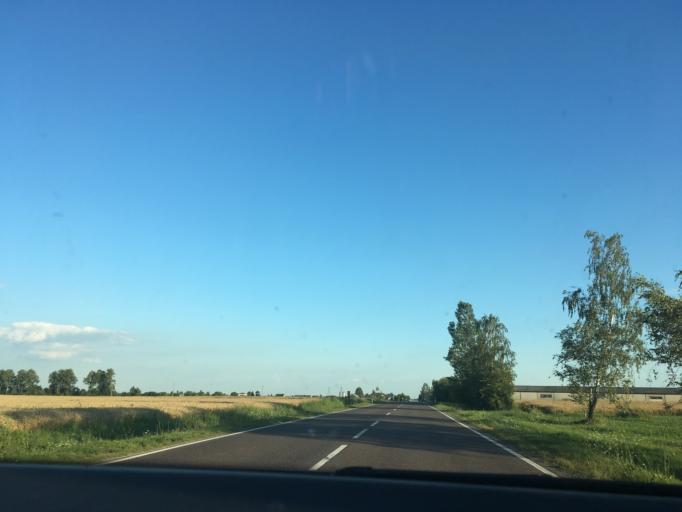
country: PL
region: Lublin Voivodeship
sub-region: Powiat bialski
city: Miedzyrzec Podlaski
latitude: 52.0399
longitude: 22.7481
